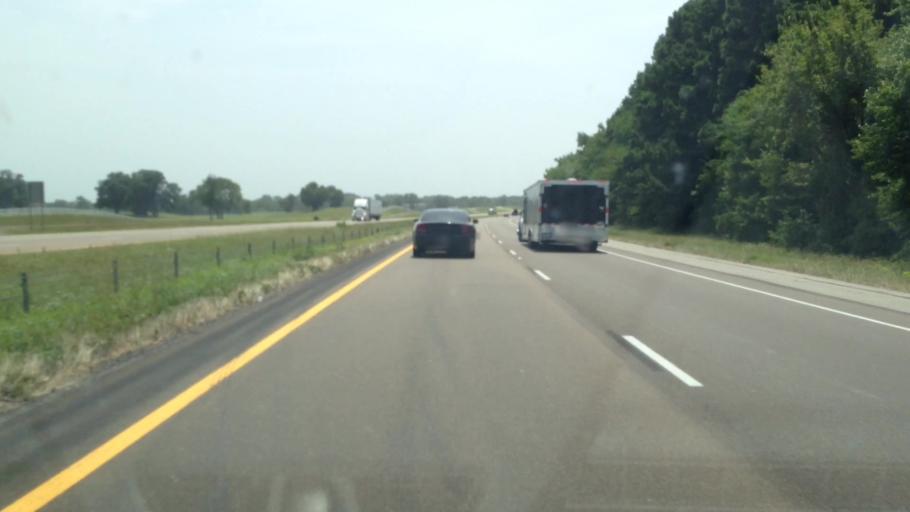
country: US
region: Texas
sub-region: Titus County
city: Mount Pleasant
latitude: 33.2030
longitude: -94.9113
